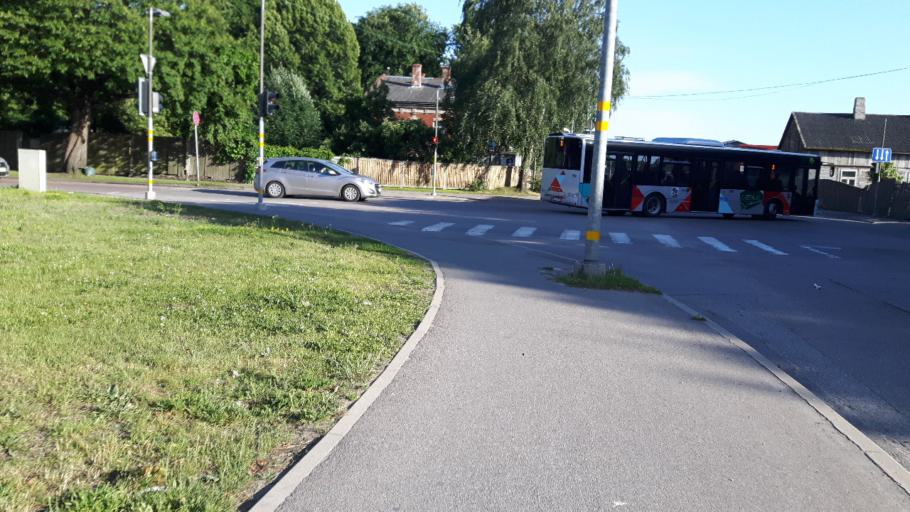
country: LV
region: Liepaja
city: Liepaja
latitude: 56.5236
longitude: 21.0046
